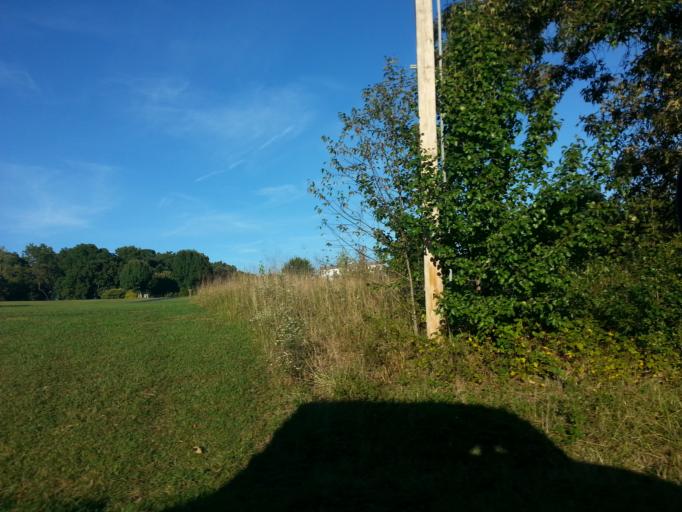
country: US
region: Tennessee
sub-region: Blount County
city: Eagleton Village
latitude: 35.7942
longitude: -83.9152
